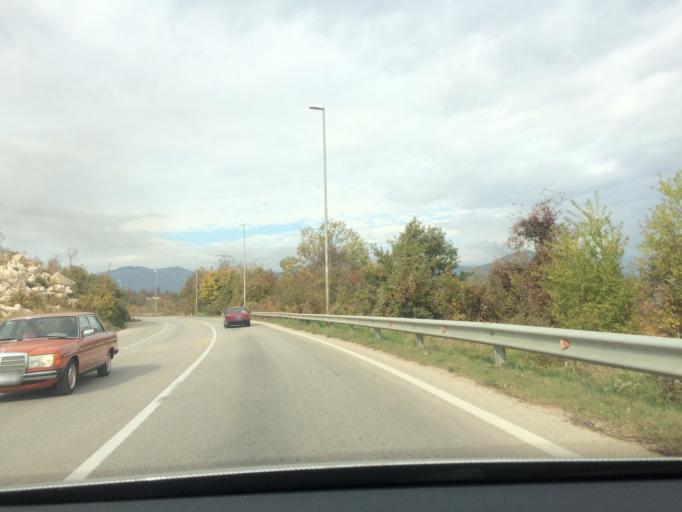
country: ME
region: Opstina Niksic
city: Niksic
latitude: 42.7805
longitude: 18.9343
